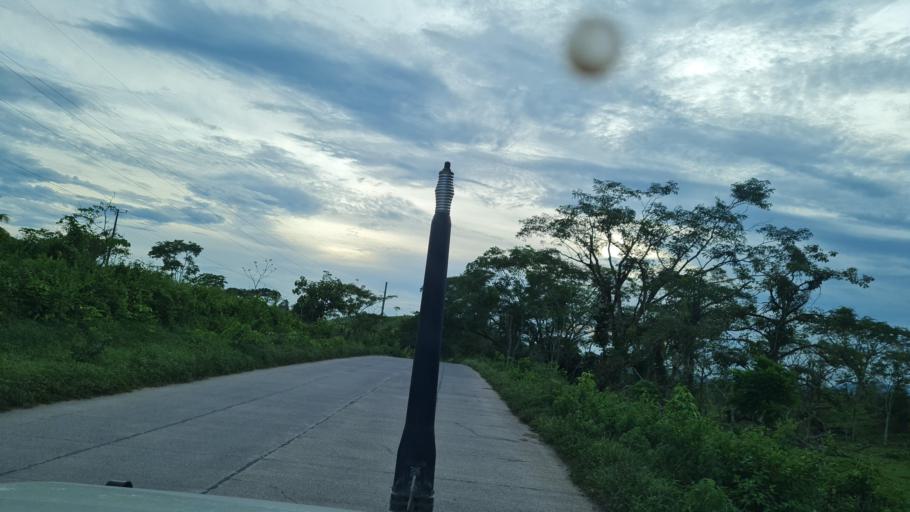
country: NI
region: Atlantico Norte (RAAN)
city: Siuna
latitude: 13.6855
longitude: -84.6049
